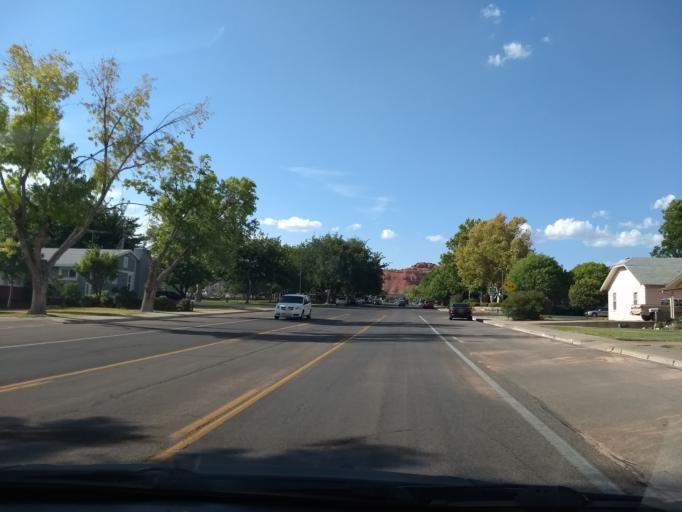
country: US
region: Utah
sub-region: Washington County
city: Saint George
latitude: 37.1024
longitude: -113.5747
